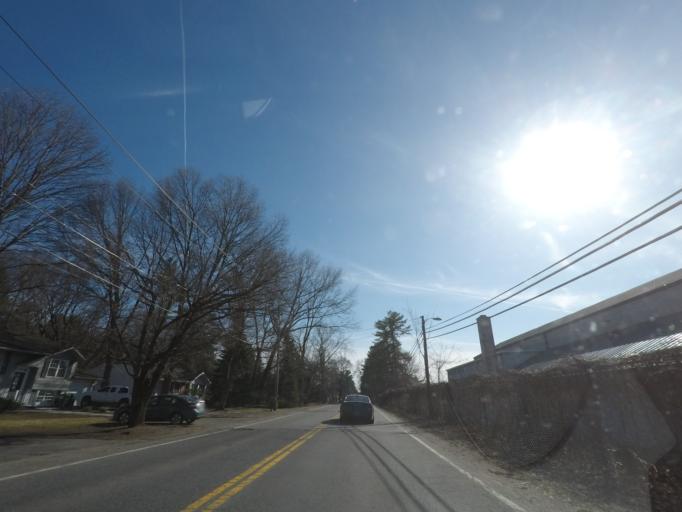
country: US
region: New York
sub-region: Saratoga County
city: Saratoga Springs
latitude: 43.0674
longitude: -73.7959
